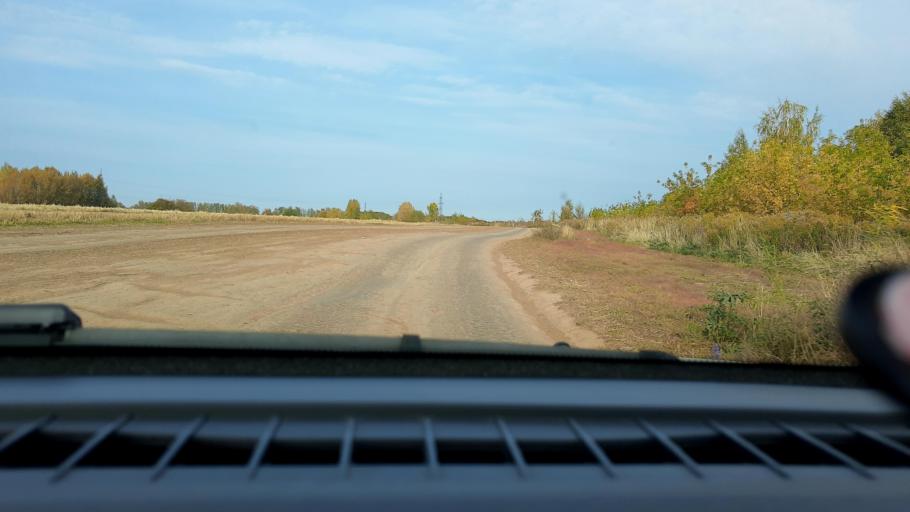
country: RU
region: Nizjnij Novgorod
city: Nizhniy Novgorod
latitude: 56.2042
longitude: 43.9658
